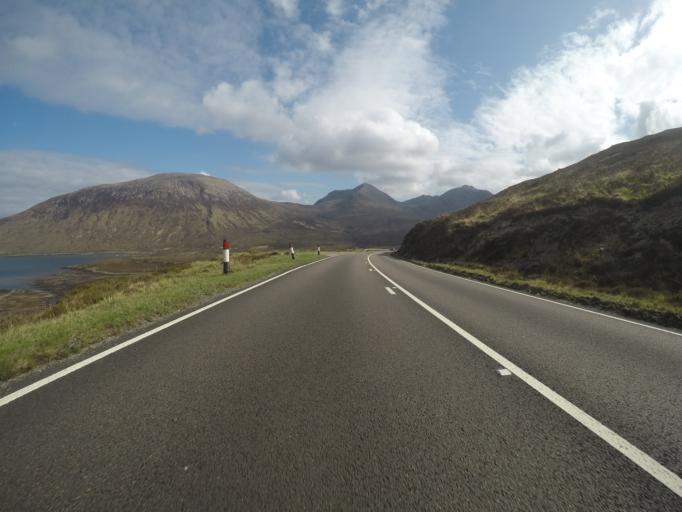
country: GB
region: Scotland
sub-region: Highland
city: Portree
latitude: 57.2725
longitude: -6.0902
